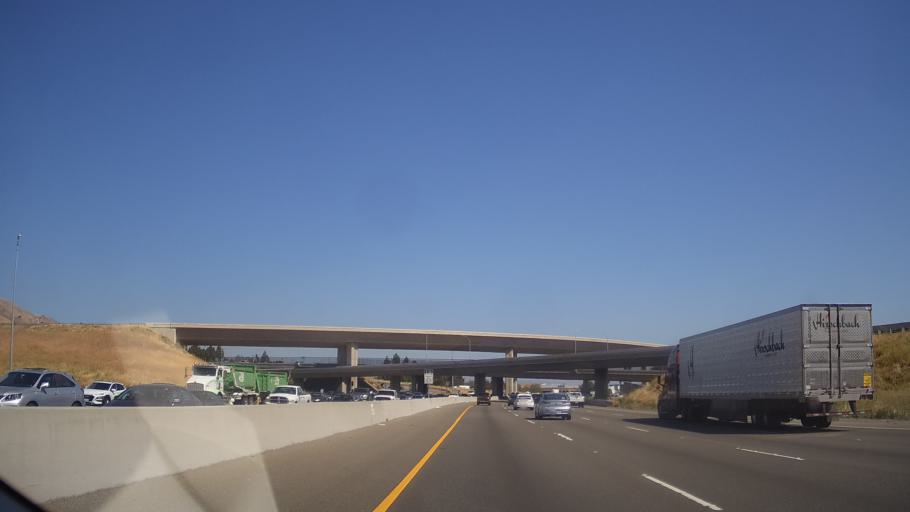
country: US
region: California
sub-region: Santa Clara County
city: Milpitas
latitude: 37.4848
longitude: -121.9398
